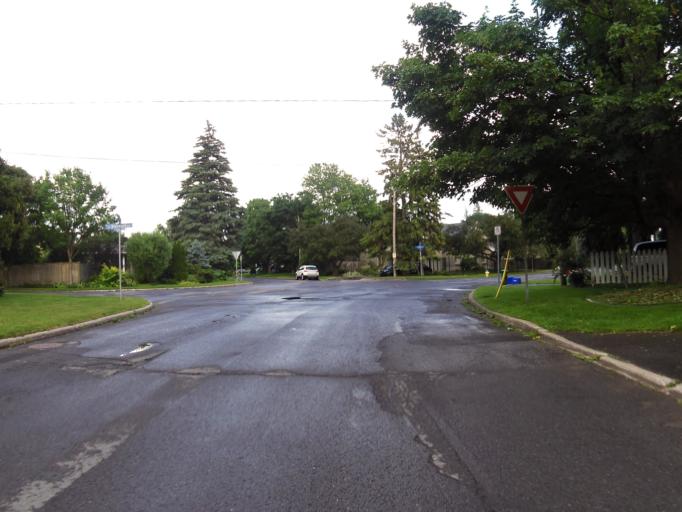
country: CA
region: Ontario
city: Ottawa
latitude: 45.3798
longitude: -75.7546
